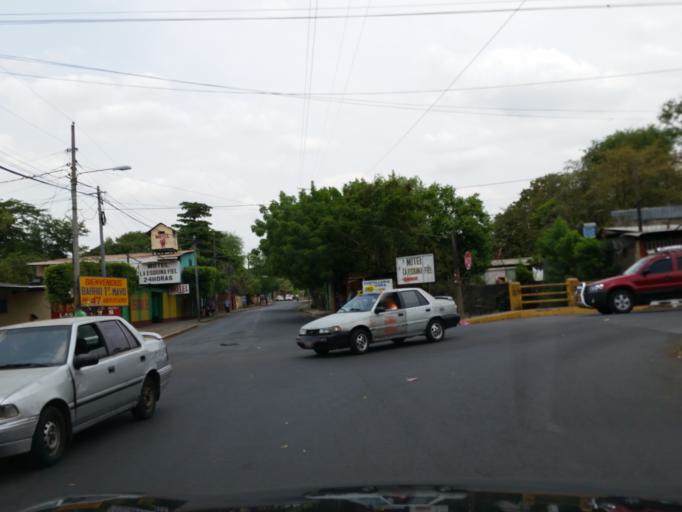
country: NI
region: Managua
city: Managua
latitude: 12.1371
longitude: -86.2330
